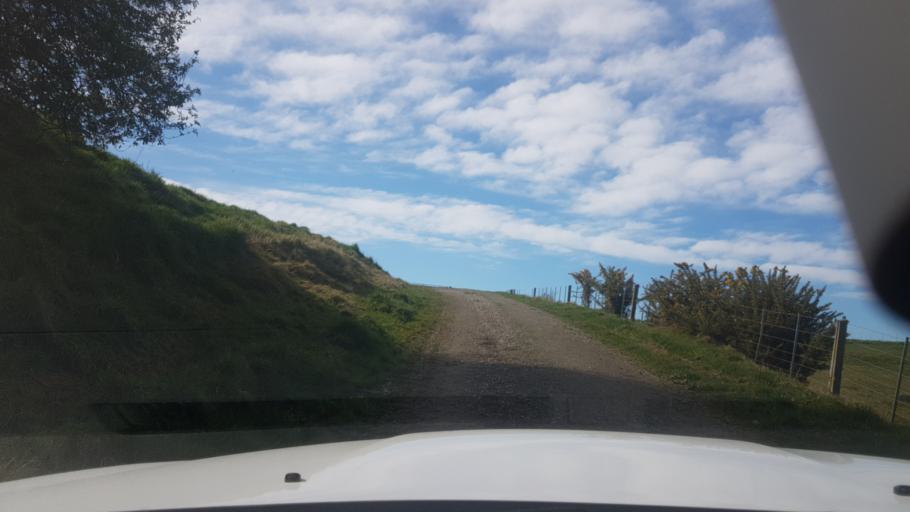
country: NZ
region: Canterbury
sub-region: Timaru District
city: Pleasant Point
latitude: -44.1957
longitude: 171.1885
